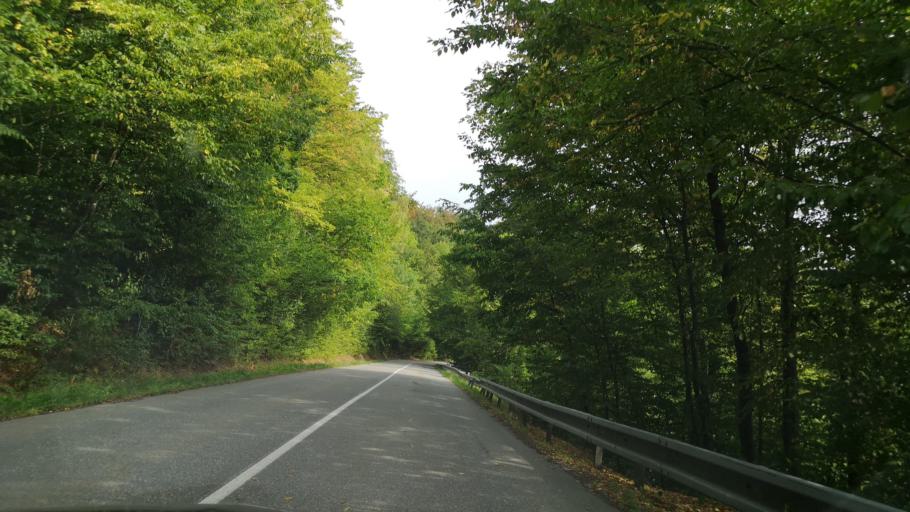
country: SK
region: Banskobystricky
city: Tisovec
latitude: 48.5744
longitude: 19.9850
